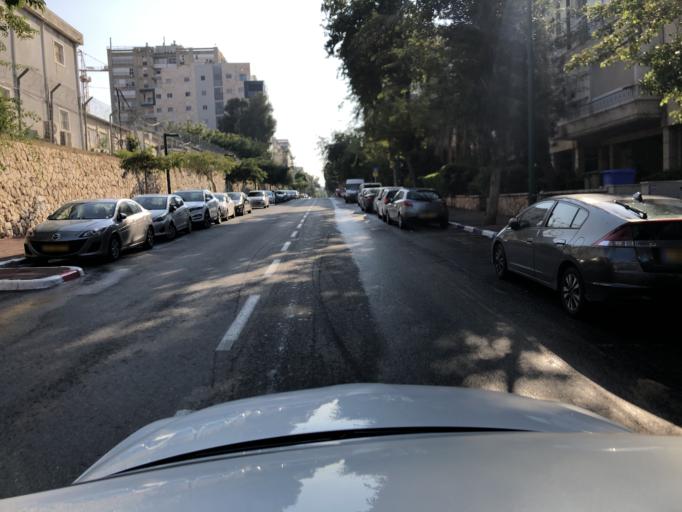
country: IL
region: Tel Aviv
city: Ramat Gan
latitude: 32.0866
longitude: 34.8200
